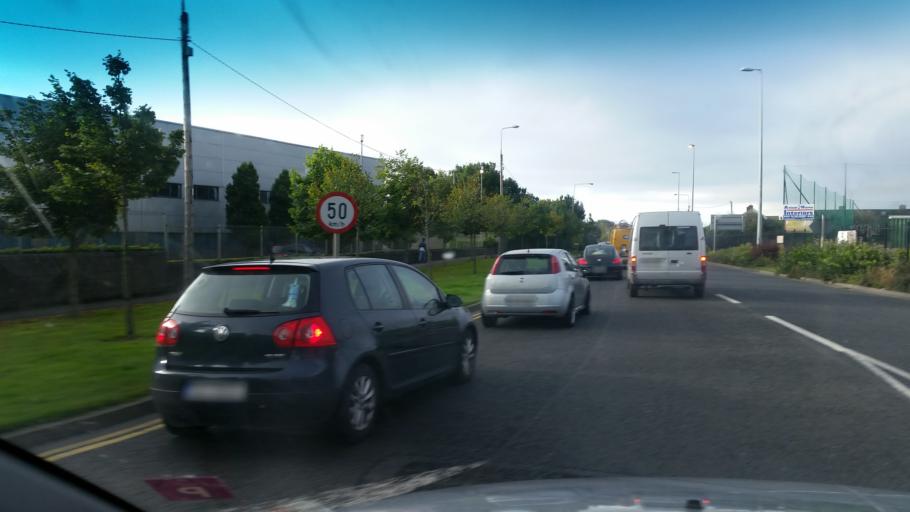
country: IE
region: Leinster
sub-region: Dublin City
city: Finglas
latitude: 53.4022
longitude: -6.3028
